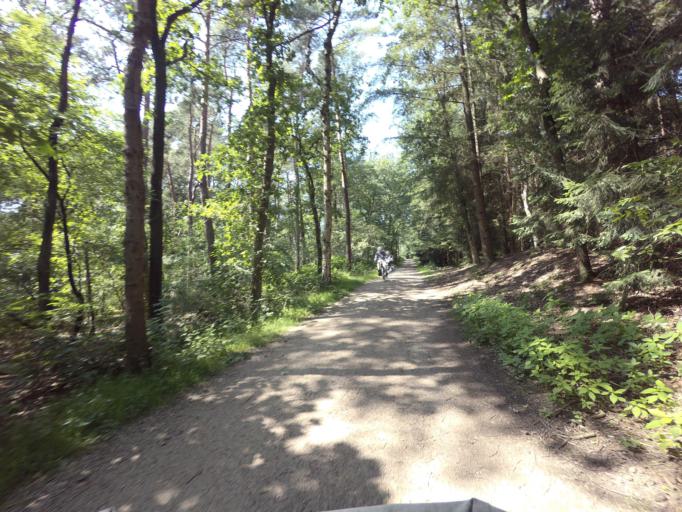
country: NL
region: Utrecht
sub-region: Gemeente Utrechtse Heuvelrug
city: Driebergen-Rijsenburg
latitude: 52.0868
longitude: 5.2780
